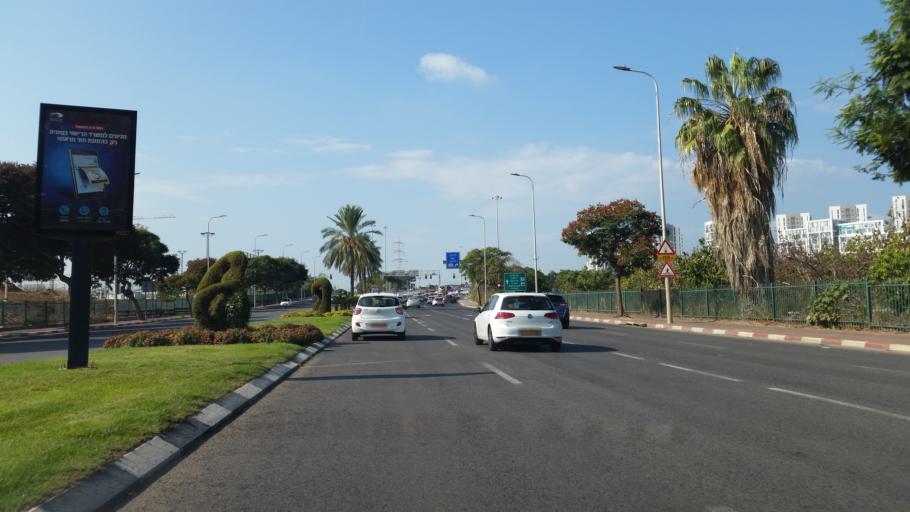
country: IL
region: Tel Aviv
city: Herzliyya
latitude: 32.1622
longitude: 34.8210
